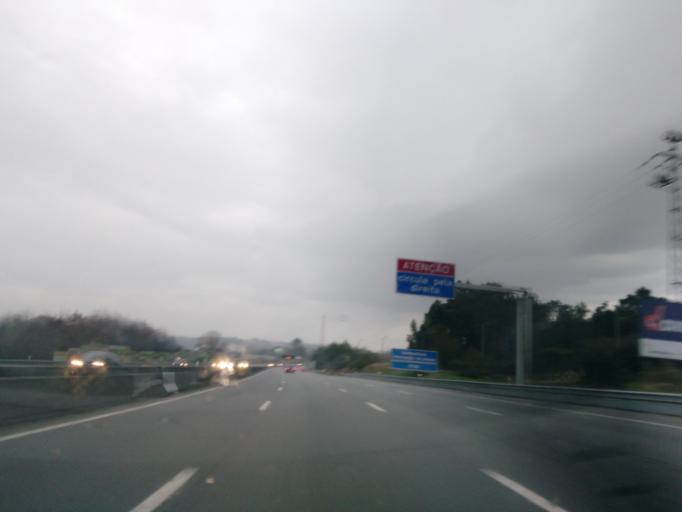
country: PT
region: Porto
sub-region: Maia
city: Aguas Santas
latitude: 41.2033
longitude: -8.5837
